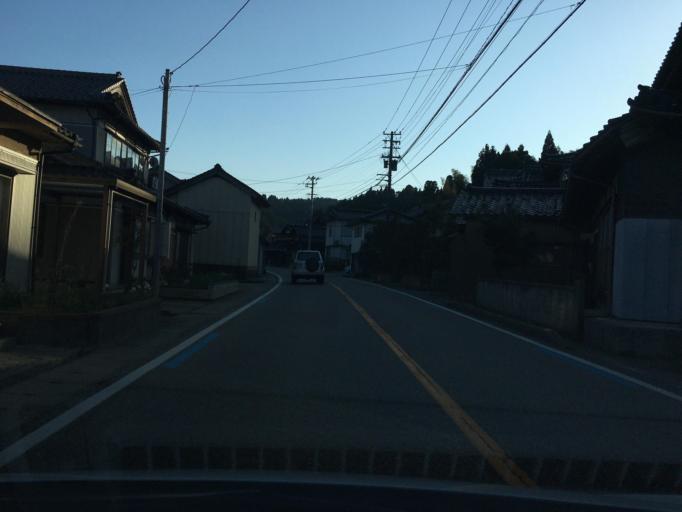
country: JP
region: Toyama
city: Himi
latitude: 36.9334
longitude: 137.0269
